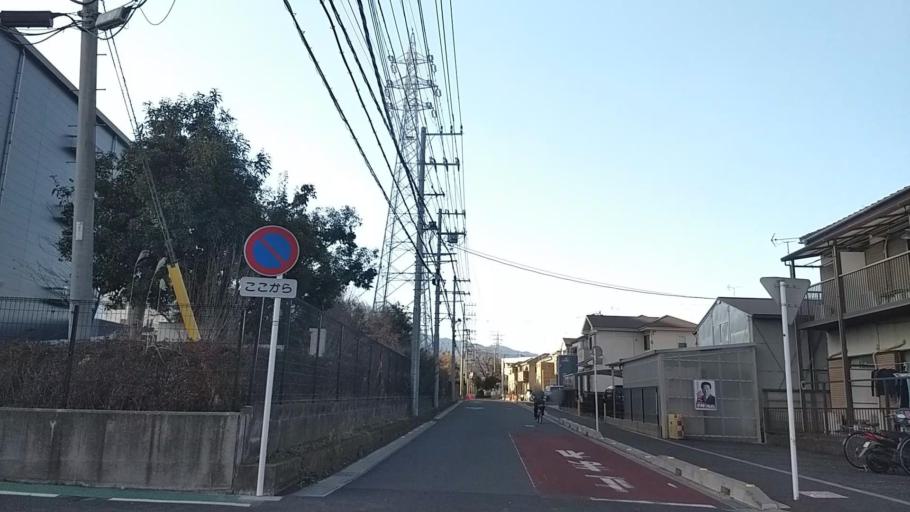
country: JP
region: Kanagawa
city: Atsugi
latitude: 35.4509
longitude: 139.3407
